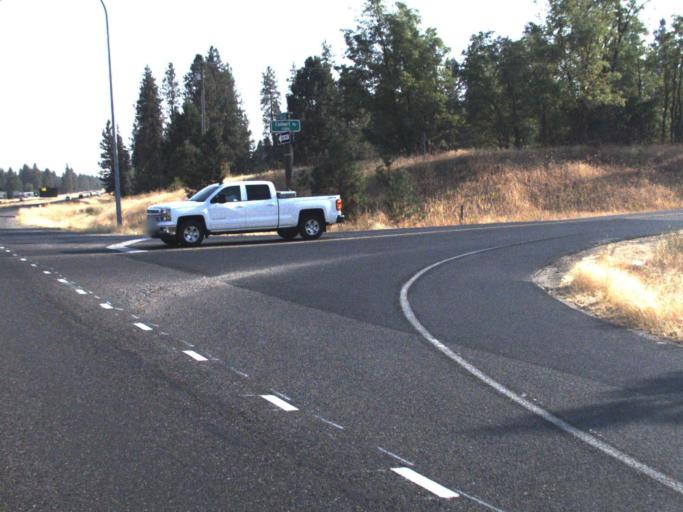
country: US
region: Washington
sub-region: Spokane County
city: Mead
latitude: 47.8247
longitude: -117.3476
